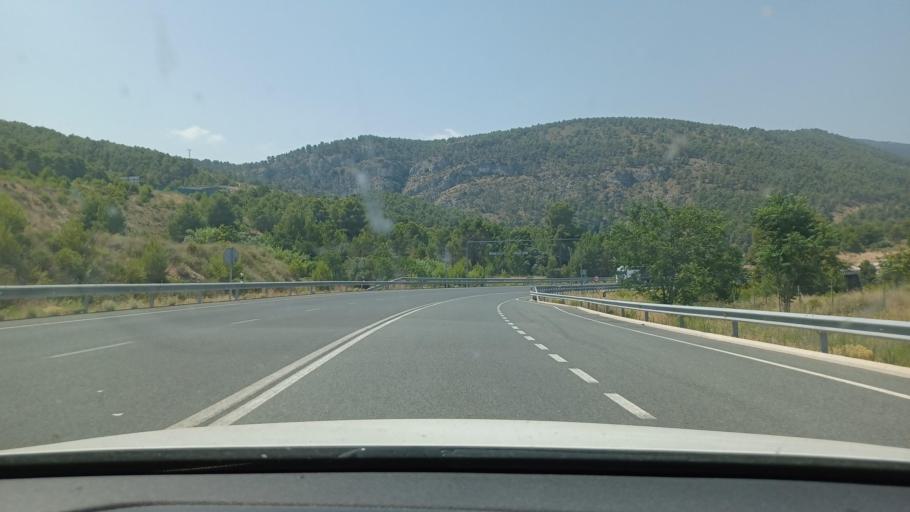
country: ES
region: Valencia
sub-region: Provincia de Alicante
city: Alcoy
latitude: 38.6818
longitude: -0.4628
